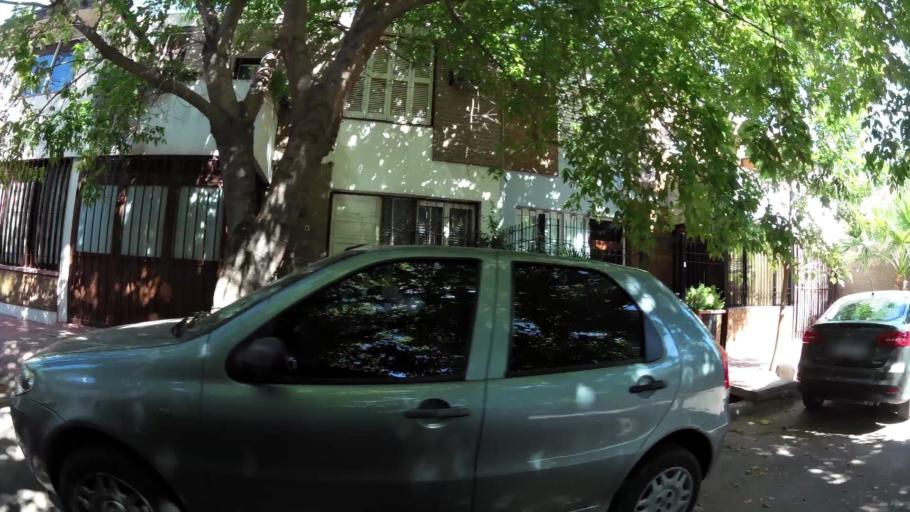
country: AR
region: Mendoza
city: Mendoza
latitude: -32.9028
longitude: -68.8578
